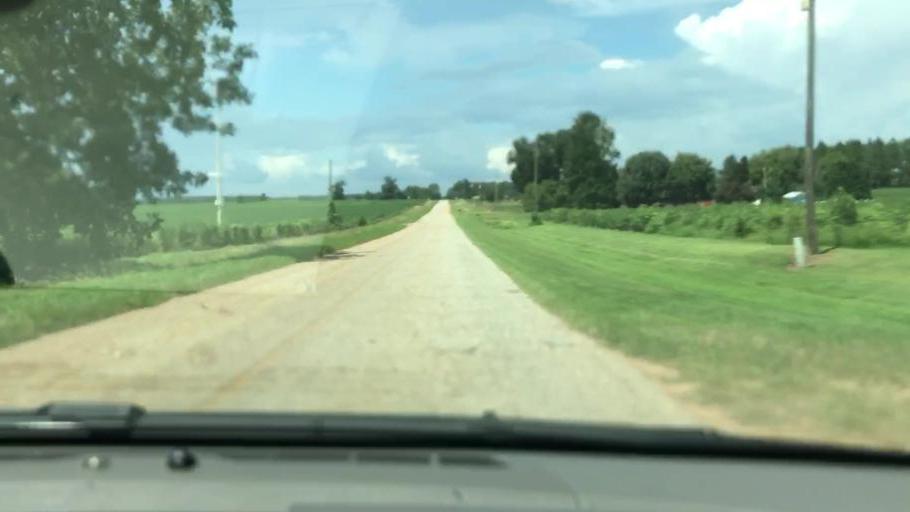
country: US
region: Georgia
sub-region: Early County
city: Blakely
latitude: 31.1942
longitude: -85.0039
